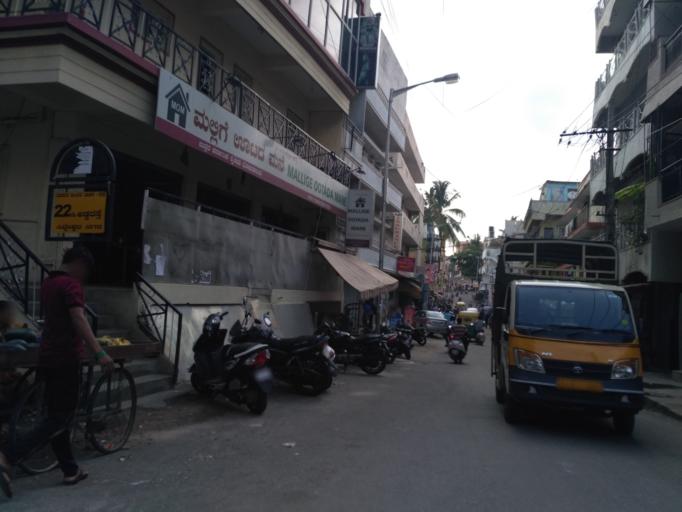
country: IN
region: Karnataka
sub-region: Bangalore Urban
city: Bangalore
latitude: 12.9680
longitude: 77.5342
